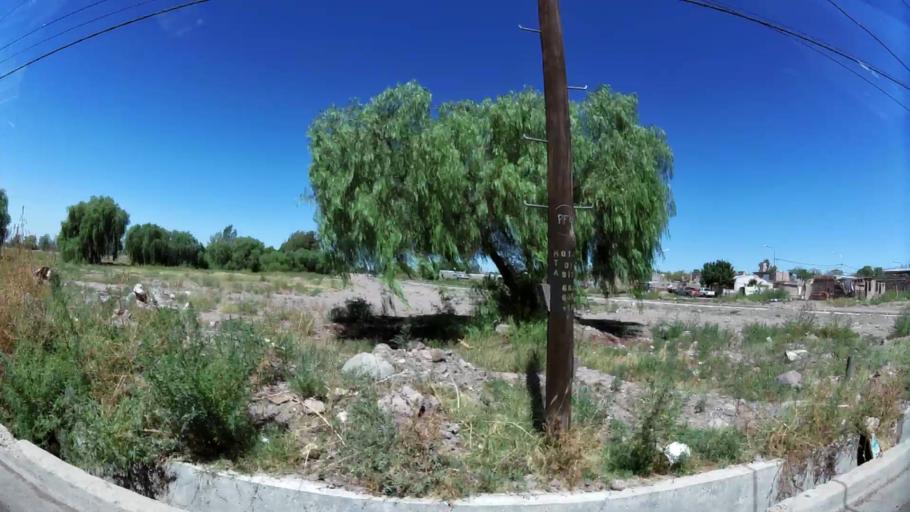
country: AR
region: Mendoza
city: Las Heras
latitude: -32.8409
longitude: -68.8627
